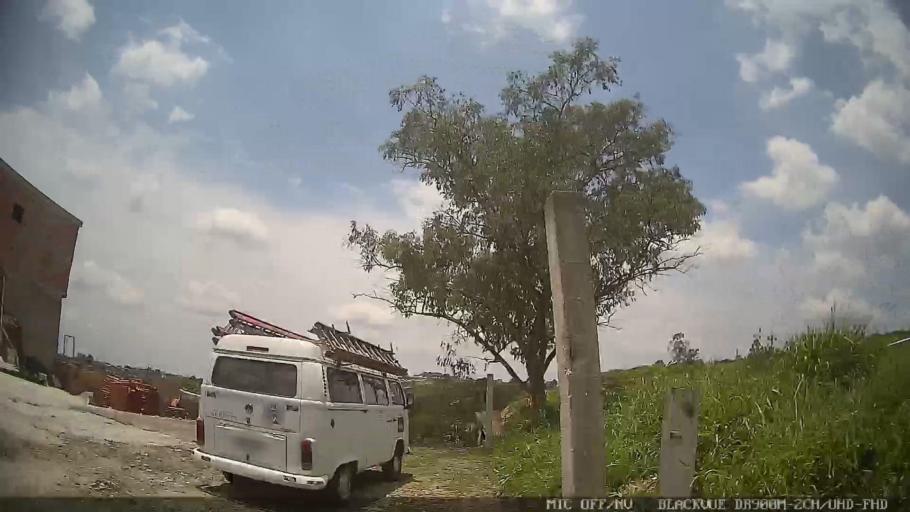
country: BR
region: Sao Paulo
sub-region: Ferraz De Vasconcelos
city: Ferraz de Vasconcelos
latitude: -23.5613
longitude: -46.3772
